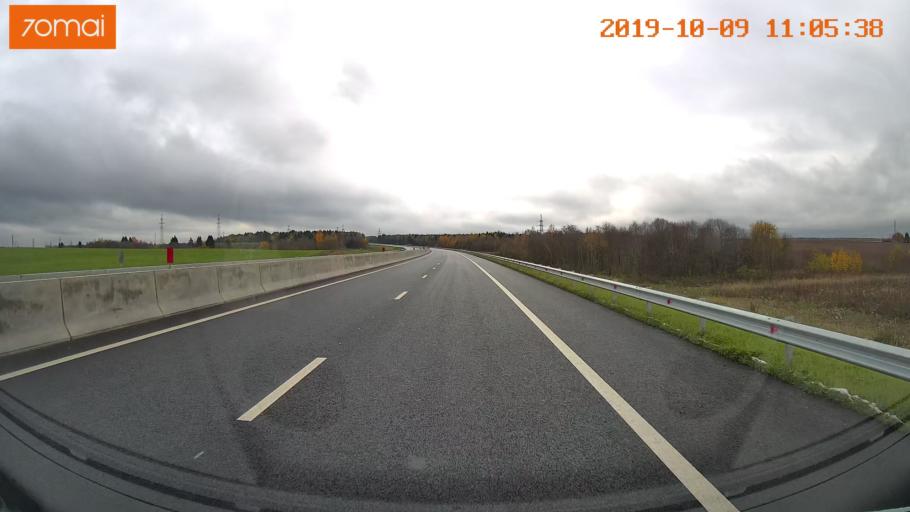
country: RU
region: Vologda
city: Molochnoye
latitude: 59.1974
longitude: 39.7580
